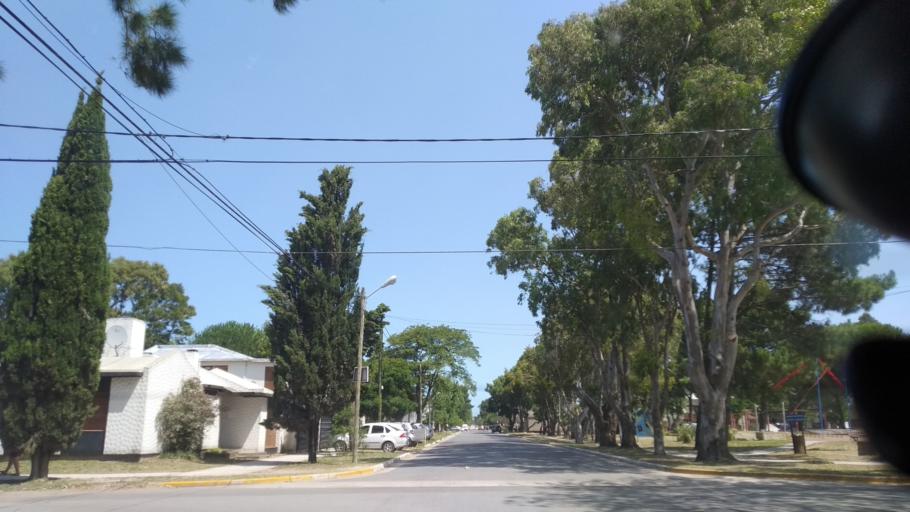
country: AR
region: Buenos Aires
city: Mar del Tuyu
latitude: -36.5773
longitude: -56.6937
